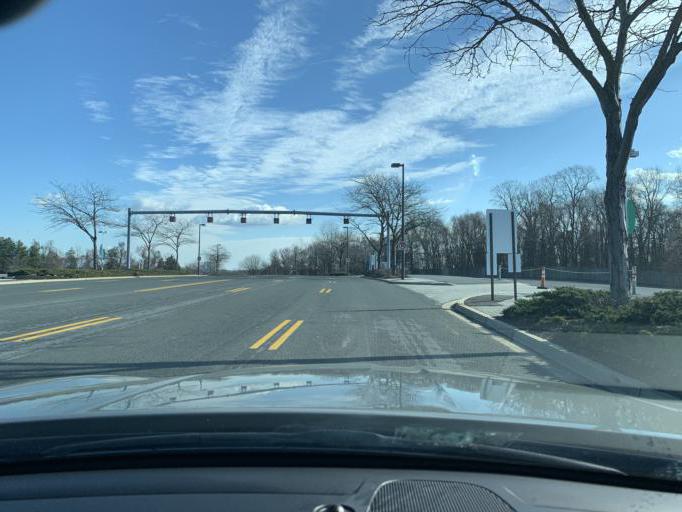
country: US
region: Maryland
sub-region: Prince George's County
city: Glenarden
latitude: 38.9061
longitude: -76.8608
